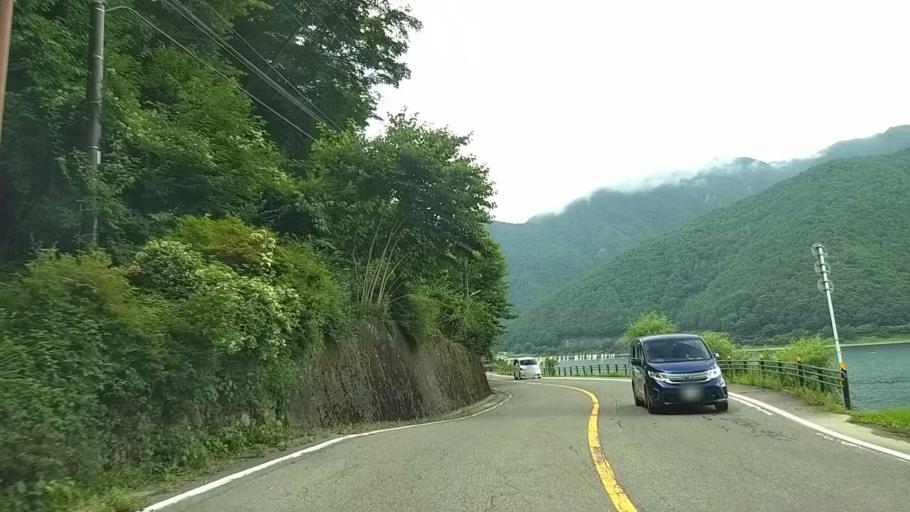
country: JP
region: Yamanashi
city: Fujikawaguchiko
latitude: 35.4965
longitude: 138.6956
